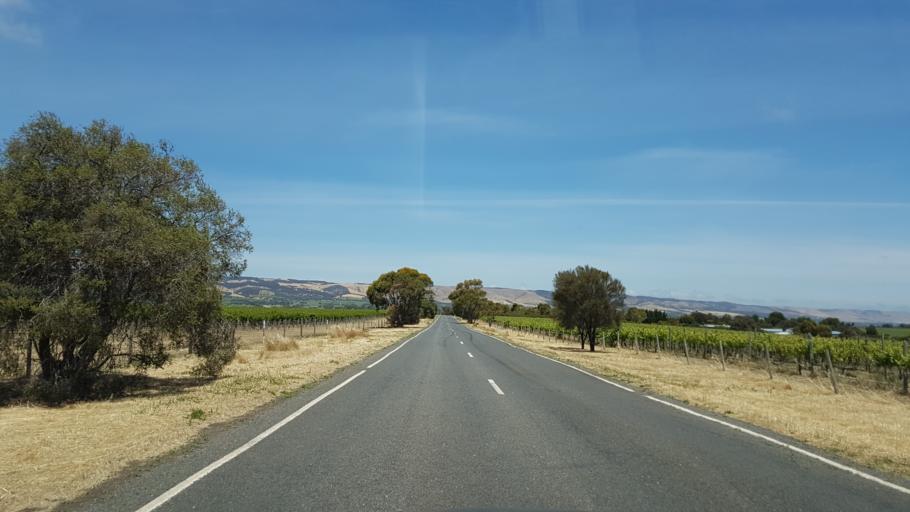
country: AU
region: South Australia
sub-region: Onkaparinga
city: McLaren Vale
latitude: -35.2368
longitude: 138.5195
